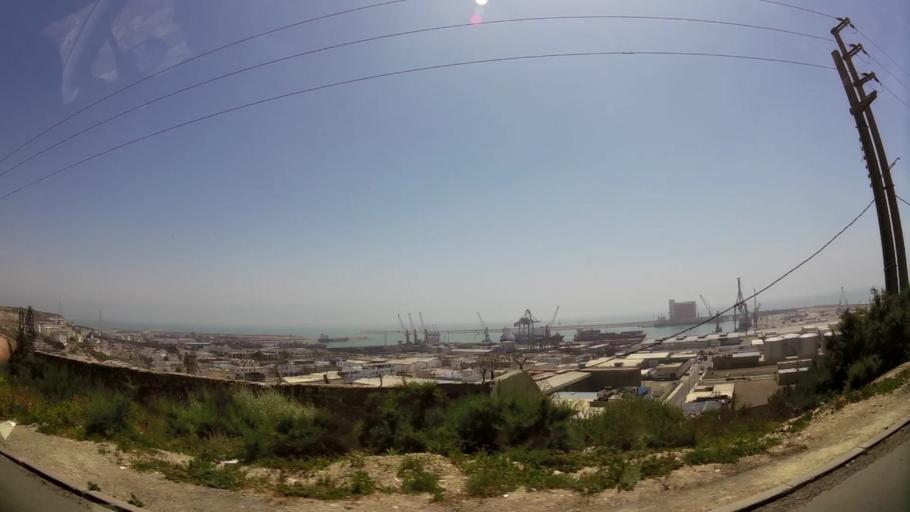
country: MA
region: Souss-Massa-Draa
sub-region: Agadir-Ida-ou-Tnan
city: Agadir
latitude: 30.4335
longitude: -9.6385
